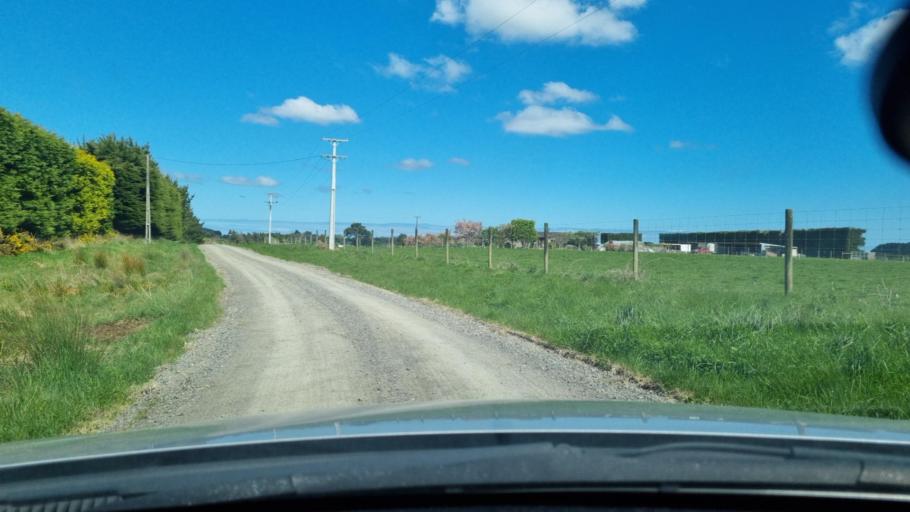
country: NZ
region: Southland
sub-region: Invercargill City
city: Invercargill
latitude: -46.3703
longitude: 168.3237
